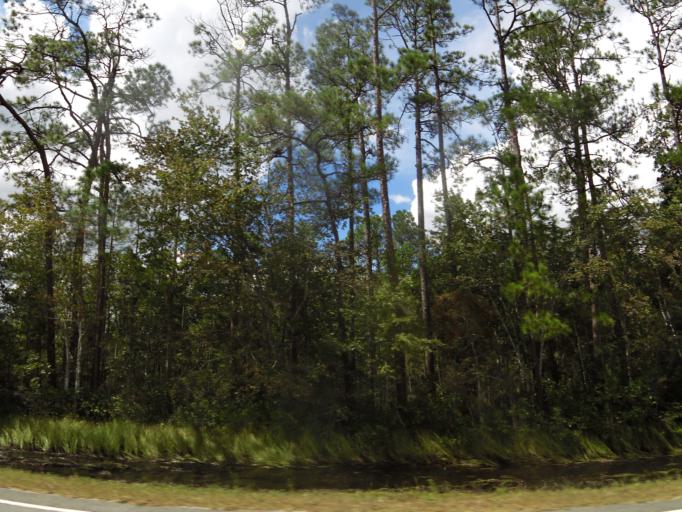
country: US
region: Georgia
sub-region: Brantley County
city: Nahunta
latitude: 31.1429
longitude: -81.9932
